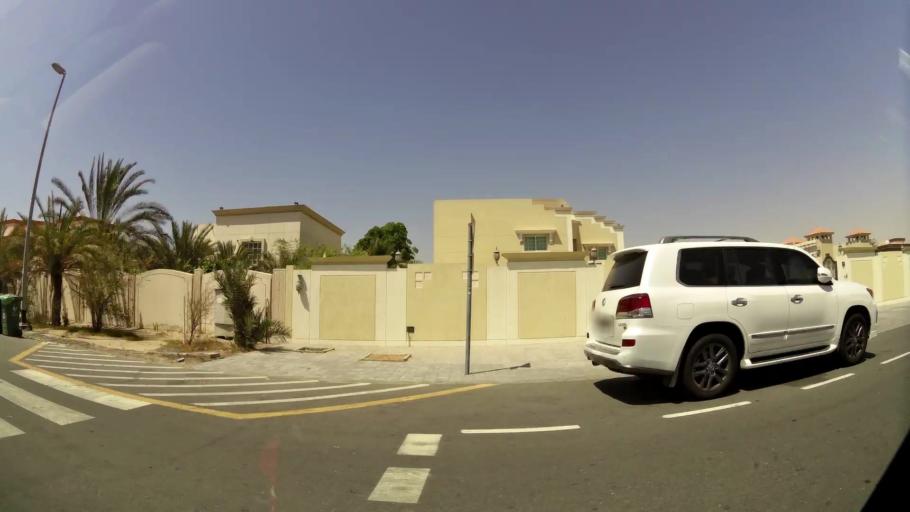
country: AE
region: Dubai
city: Dubai
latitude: 25.1027
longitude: 55.2117
